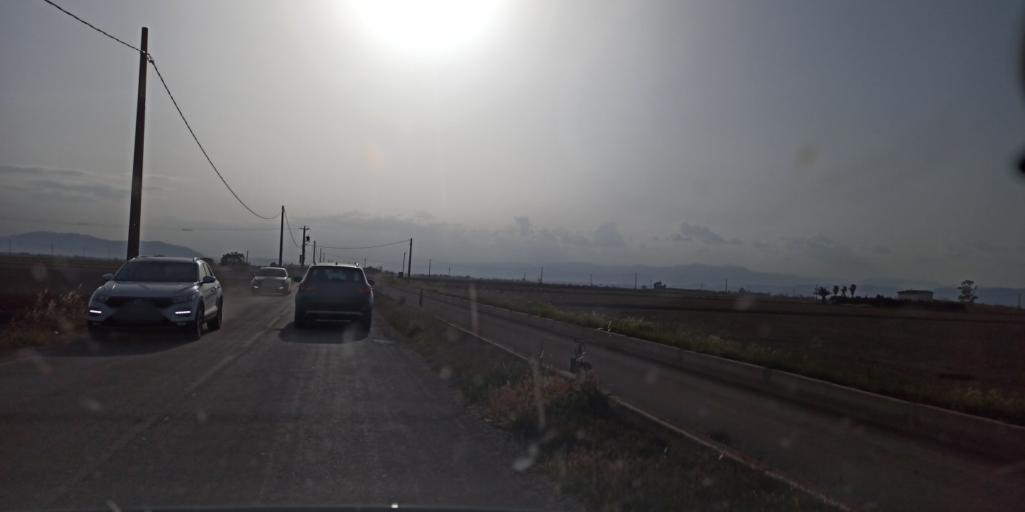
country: ES
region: Catalonia
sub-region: Provincia de Tarragona
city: Deltebre
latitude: 40.7509
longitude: 0.7761
